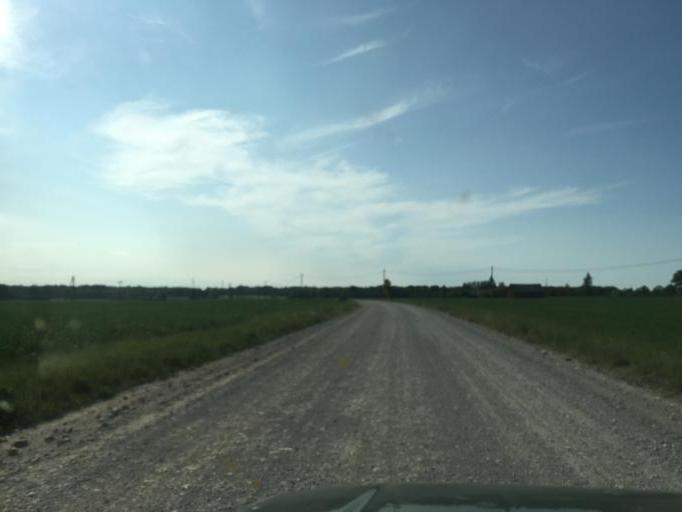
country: LV
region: Dundaga
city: Dundaga
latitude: 57.6223
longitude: 22.4092
